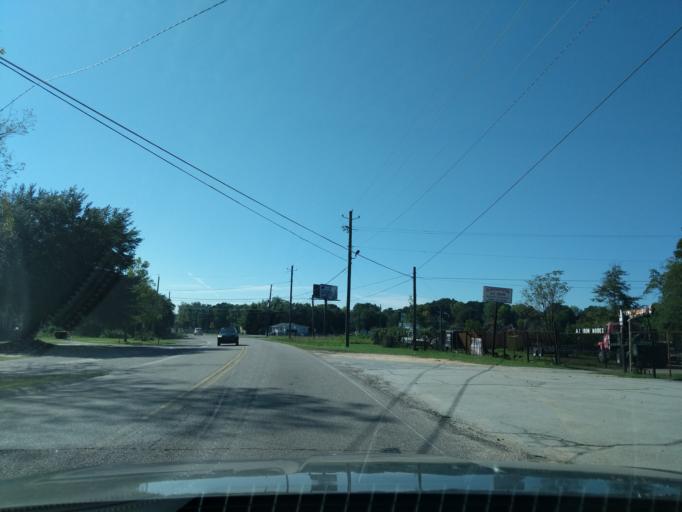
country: US
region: Georgia
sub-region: Richmond County
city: Augusta
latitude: 33.4316
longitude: -82.0060
